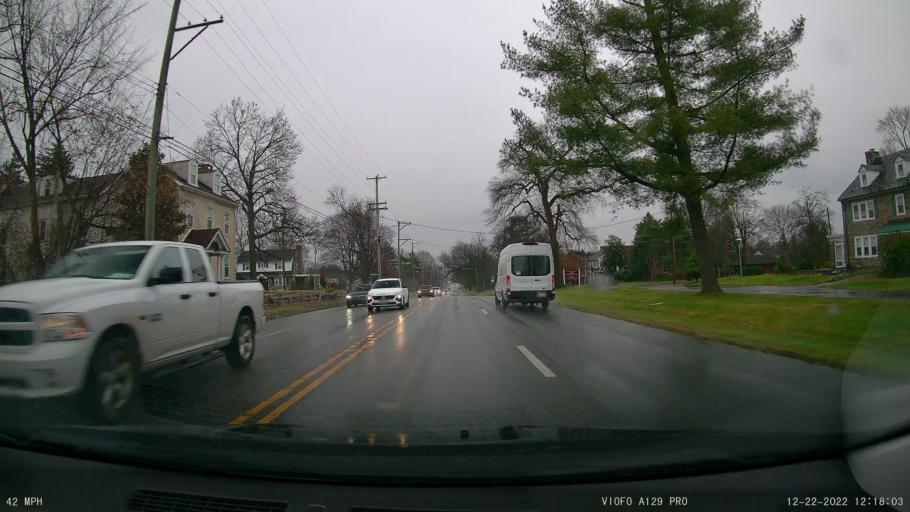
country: US
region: Pennsylvania
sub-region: Montgomery County
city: West Norriton
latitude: 40.1279
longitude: -75.3701
